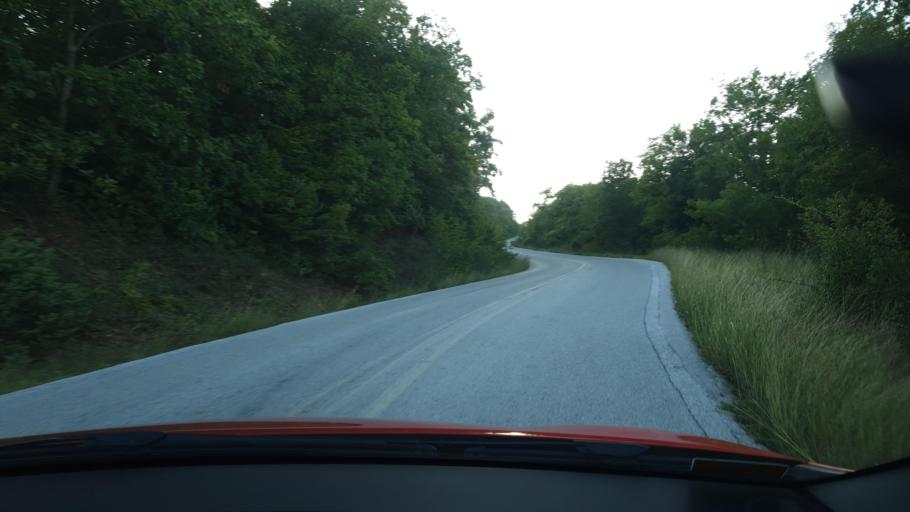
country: GR
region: Central Macedonia
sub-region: Nomos Chalkidikis
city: Galatista
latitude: 40.5405
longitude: 23.2853
